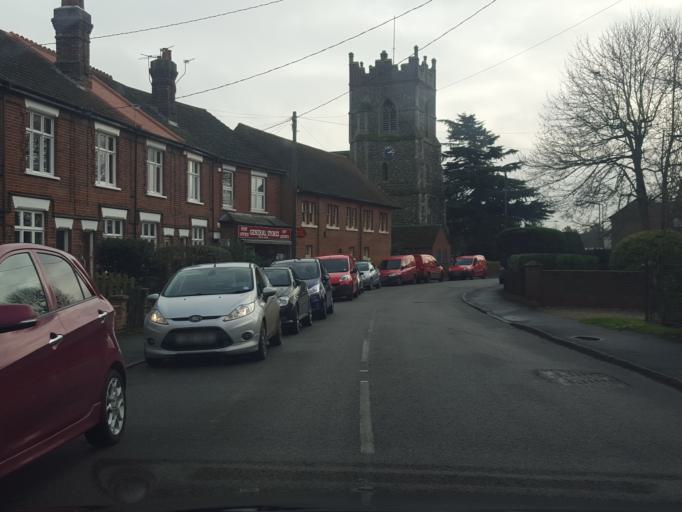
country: GB
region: England
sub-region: Suffolk
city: East Bergholt
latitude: 51.9274
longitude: 0.9853
